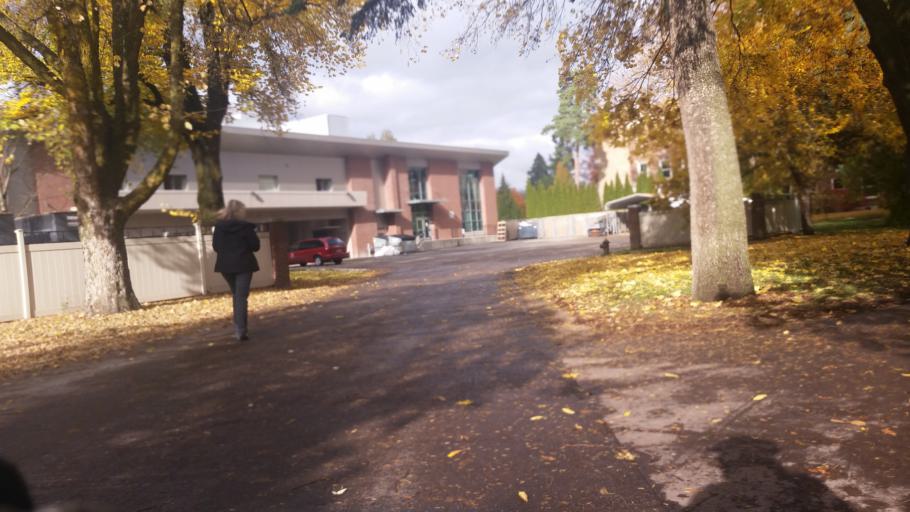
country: US
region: Washington
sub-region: Spokane County
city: Cheney
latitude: 47.4905
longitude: -117.5811
